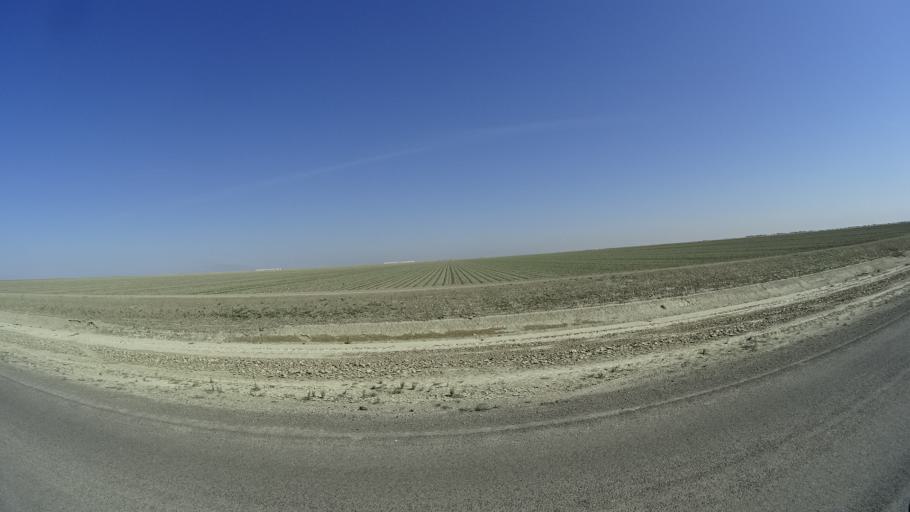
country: US
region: California
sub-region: Tulare County
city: Alpaugh
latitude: 35.8914
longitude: -119.5443
